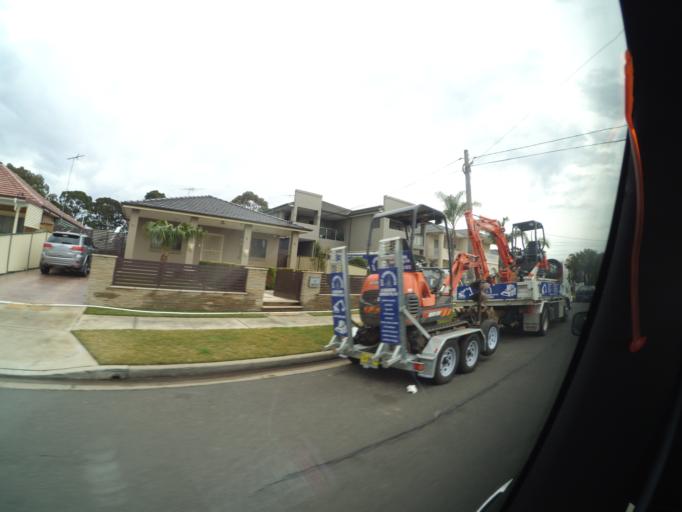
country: AU
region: New South Wales
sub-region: Bankstown
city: Bankstown
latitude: -33.9247
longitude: 151.0250
